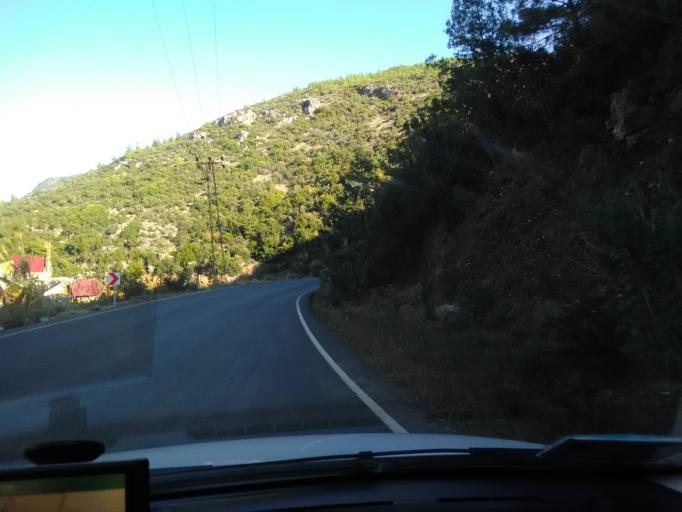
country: TR
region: Antalya
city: Gazipasa
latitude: 36.2801
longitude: 32.3615
